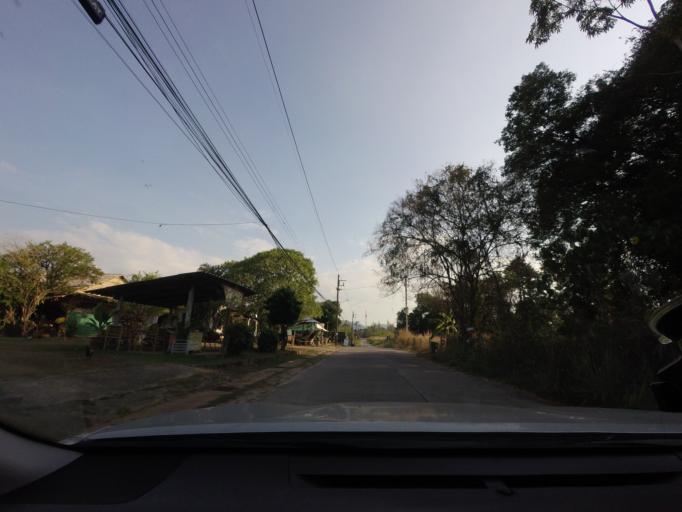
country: TH
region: Phangnga
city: Ban Khao Lak
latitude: 8.6940
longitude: 98.2513
